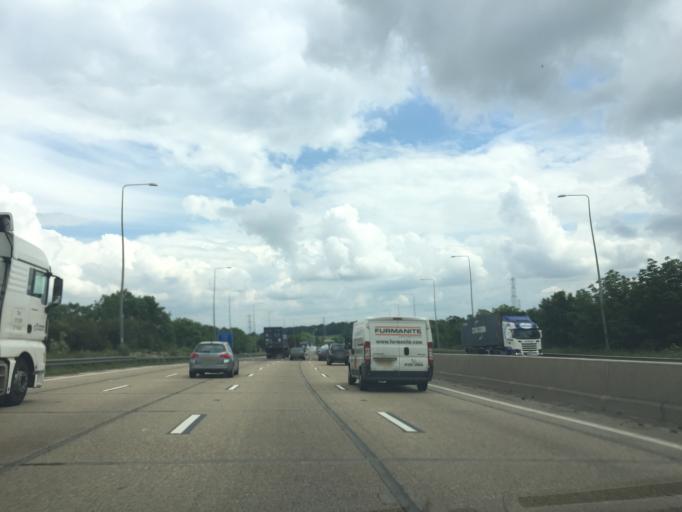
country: GB
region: England
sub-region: Hertfordshire
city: Potters Bar
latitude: 51.6876
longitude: -0.1607
